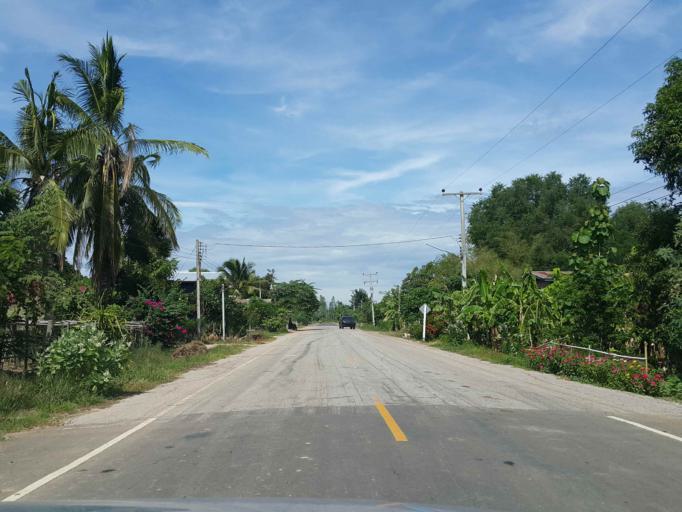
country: TH
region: Sukhothai
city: Ban Dan Lan Hoi
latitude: 17.1136
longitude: 99.5114
